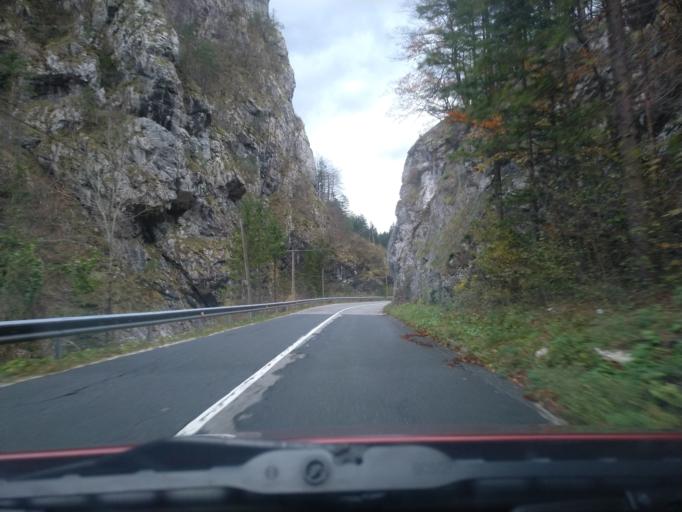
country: SI
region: Luce
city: Luce
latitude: 46.3822
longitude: 14.7264
